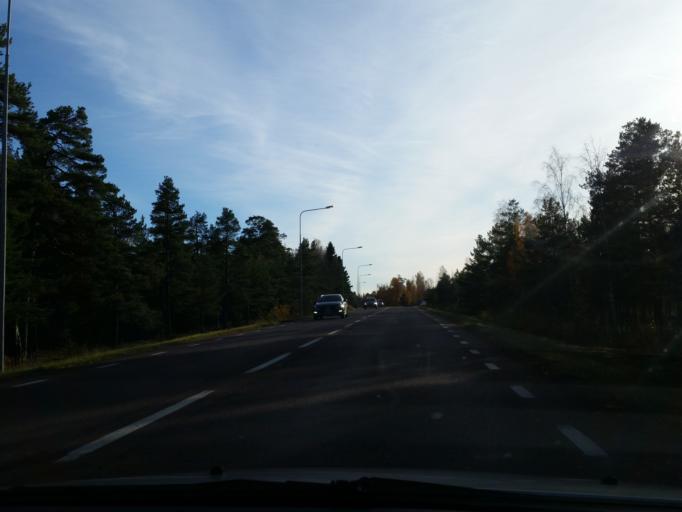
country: AX
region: Alands landsbygd
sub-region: Jomala
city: Jomala
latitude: 60.1266
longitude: 19.9340
